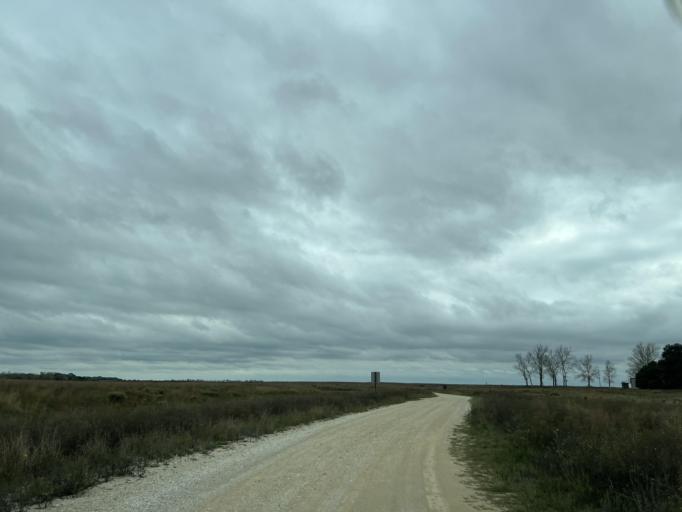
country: US
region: Texas
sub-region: Colorado County
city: Eagle Lake
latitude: 29.6710
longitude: -96.2669
